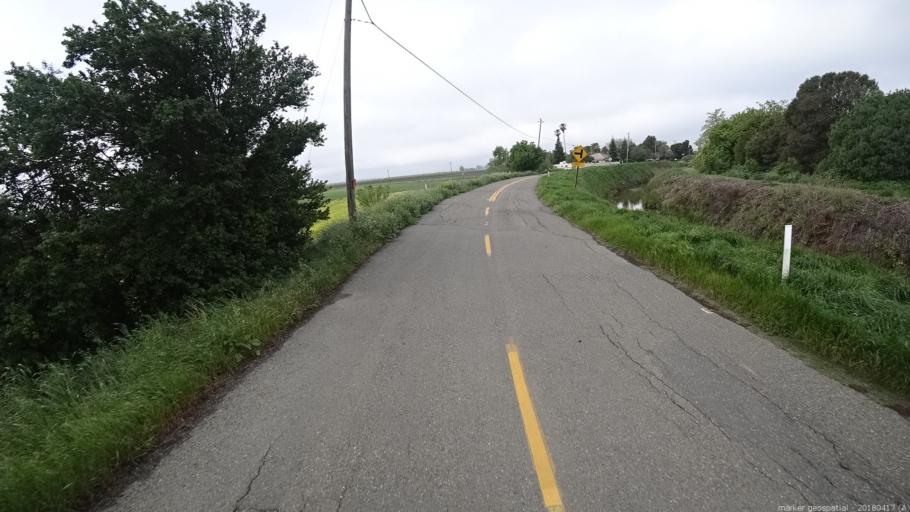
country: US
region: California
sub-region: Sacramento County
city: Walnut Grove
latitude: 38.2106
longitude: -121.5931
